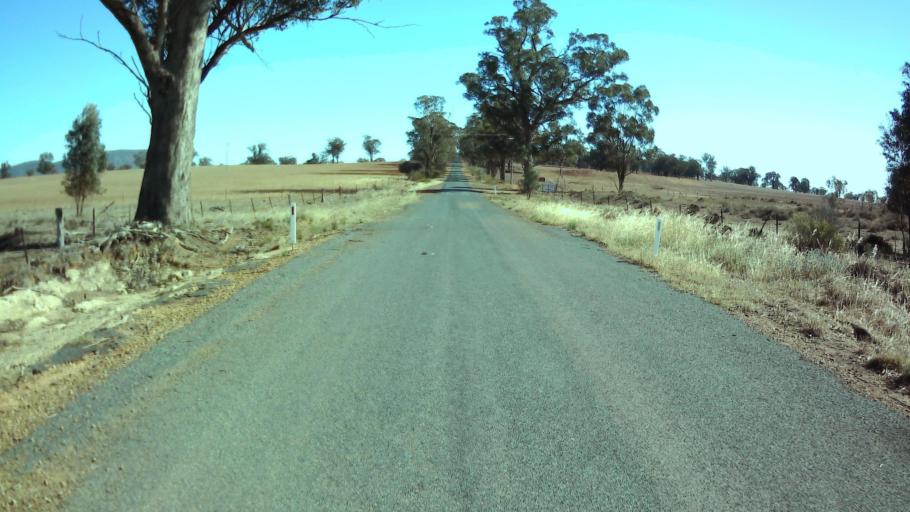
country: AU
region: New South Wales
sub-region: Weddin
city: Grenfell
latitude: -33.7920
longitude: 147.9573
